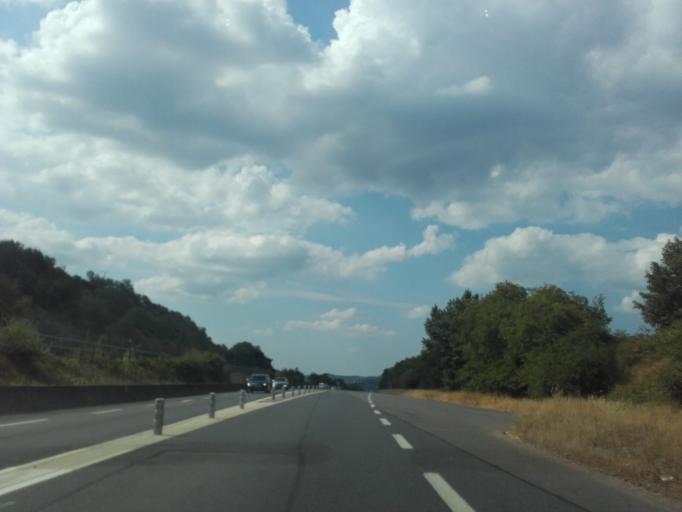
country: FR
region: Bourgogne
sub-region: Departement de Saone-et-Loire
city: Prisse
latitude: 46.3222
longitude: 4.7388
